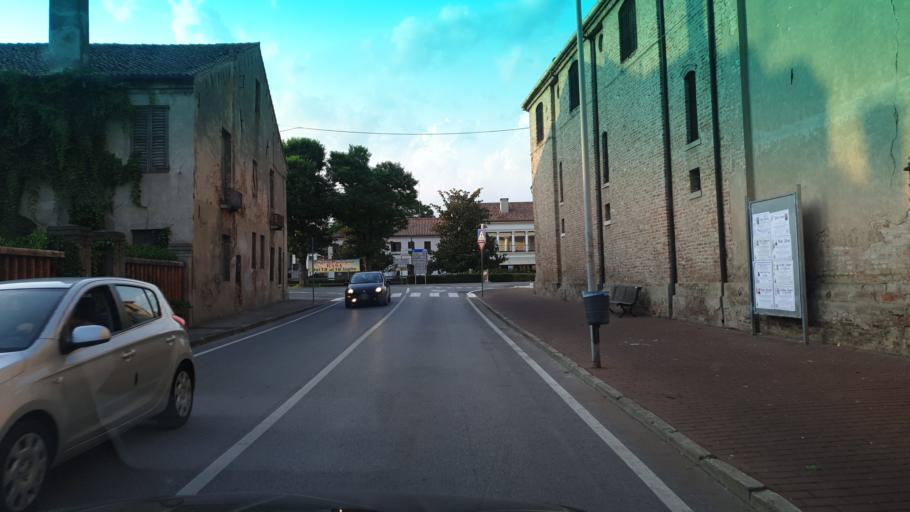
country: IT
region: Veneto
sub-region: Provincia di Rovigo
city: Lendinara
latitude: 45.0824
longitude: 11.5978
